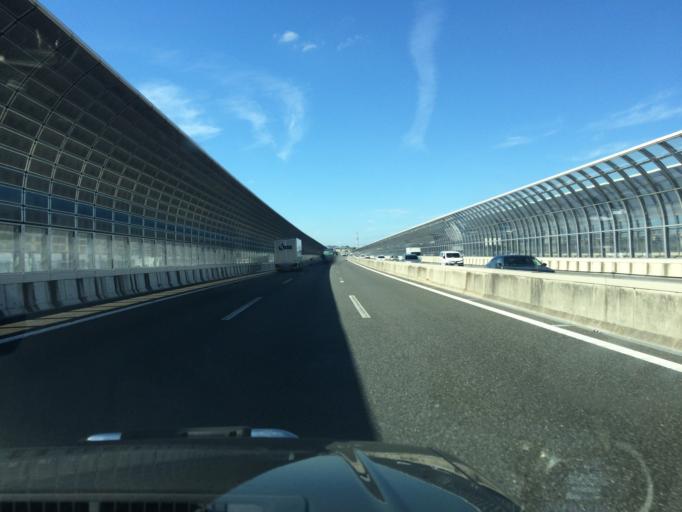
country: JP
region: Osaka
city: Hirakata
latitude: 34.7852
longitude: 135.6862
